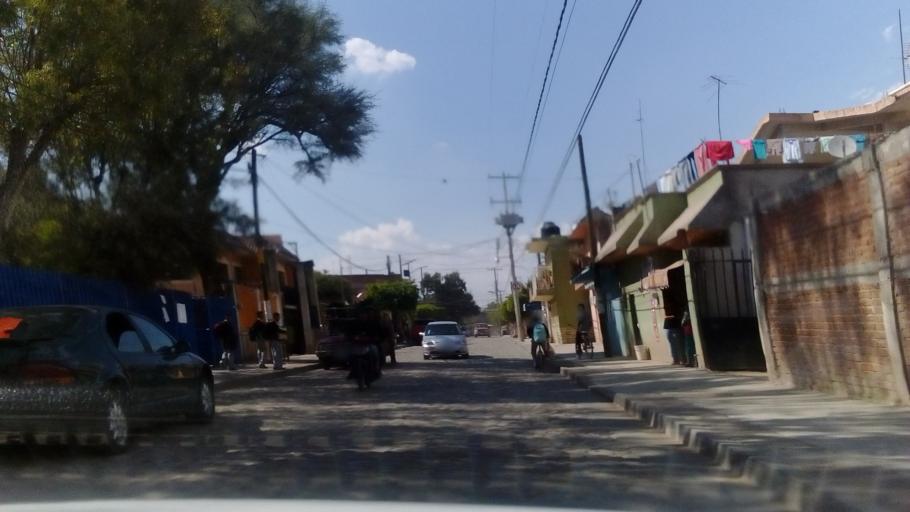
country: MX
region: Guanajuato
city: Duarte
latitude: 21.0862
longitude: -101.5212
